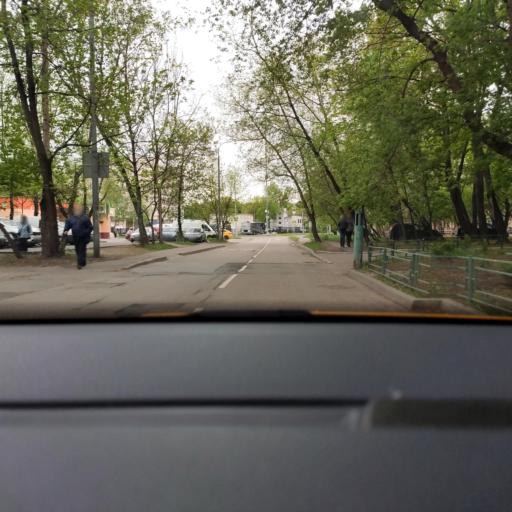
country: RU
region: Moscow
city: Perovo
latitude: 55.7471
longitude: 37.7946
